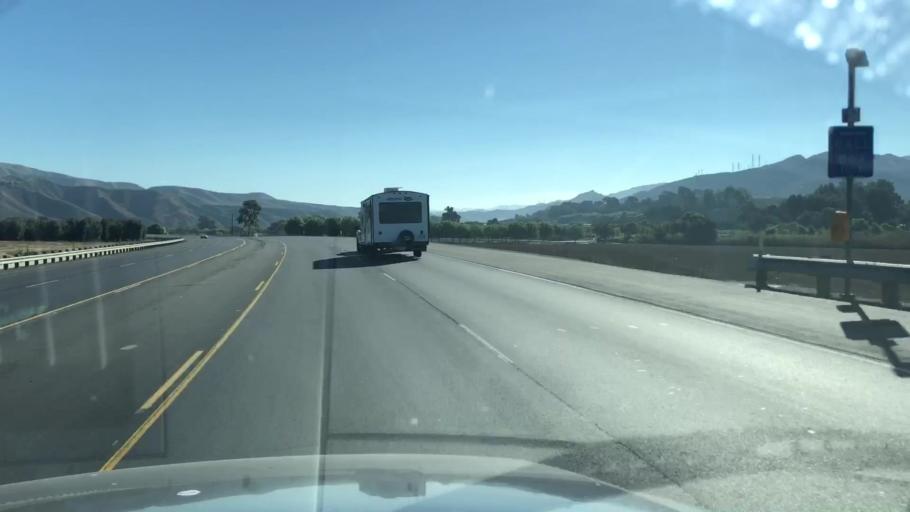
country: US
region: California
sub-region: Ventura County
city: Piru
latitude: 34.4056
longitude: -118.7441
